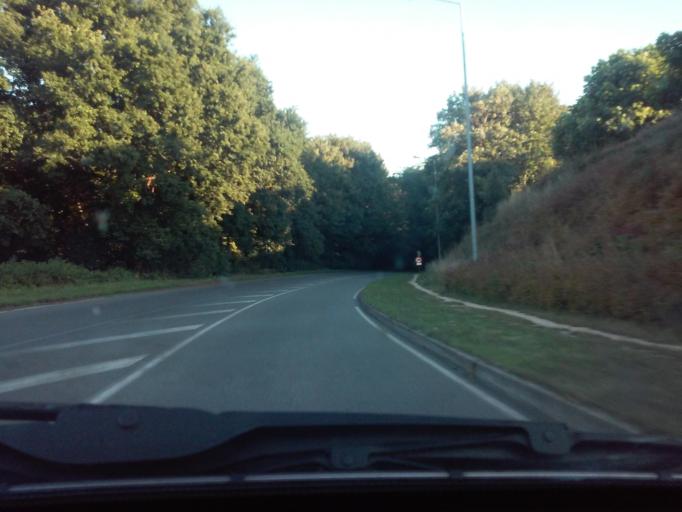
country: FR
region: Brittany
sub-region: Departement des Cotes-d'Armor
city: Lanvallay
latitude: 48.4682
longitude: -2.0429
